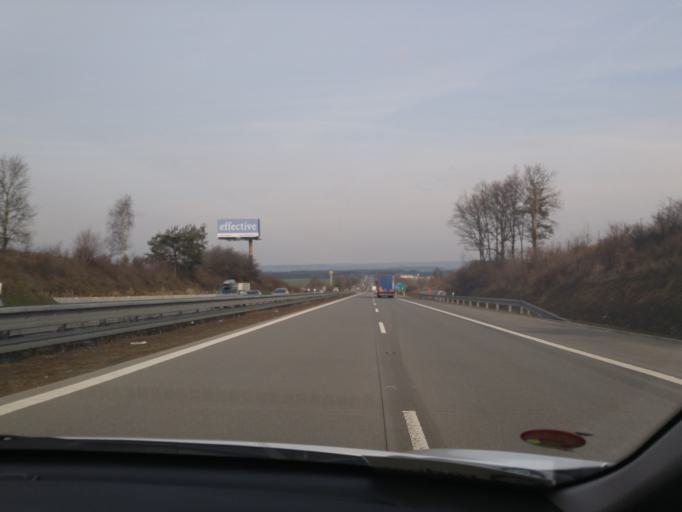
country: CZ
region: Central Bohemia
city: Cechtice
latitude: 49.6515
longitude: 15.1234
